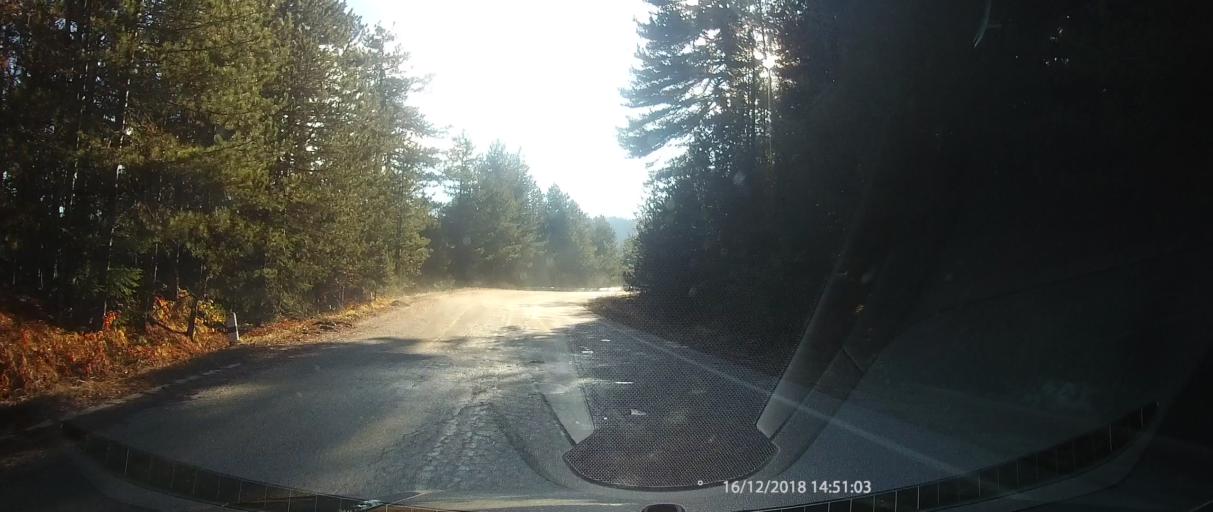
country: GR
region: West Macedonia
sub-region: Nomos Kastorias
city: Nestorio
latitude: 40.2075
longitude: 21.0744
